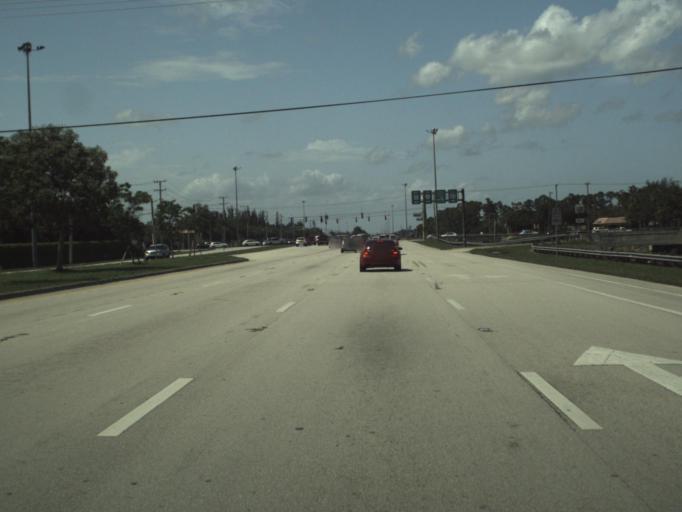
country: US
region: Florida
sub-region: Palm Beach County
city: Wellington
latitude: 26.6149
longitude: -80.2049
